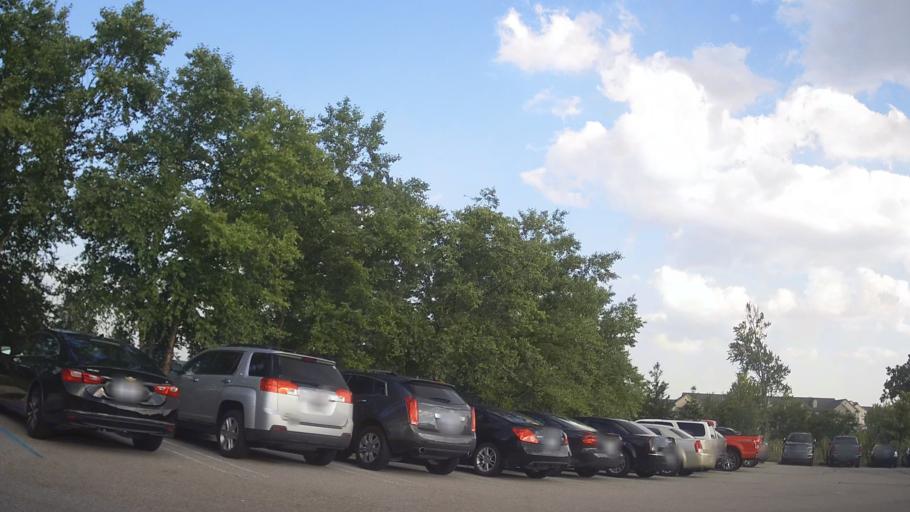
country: US
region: Michigan
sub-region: Macomb County
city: Clinton
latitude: 42.6246
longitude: -82.9450
